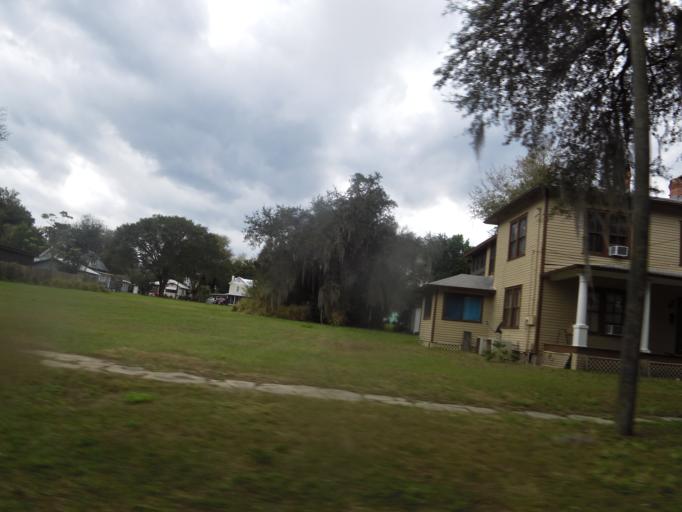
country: US
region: Florida
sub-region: Putnam County
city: Crescent City
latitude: 29.4325
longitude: -81.5082
